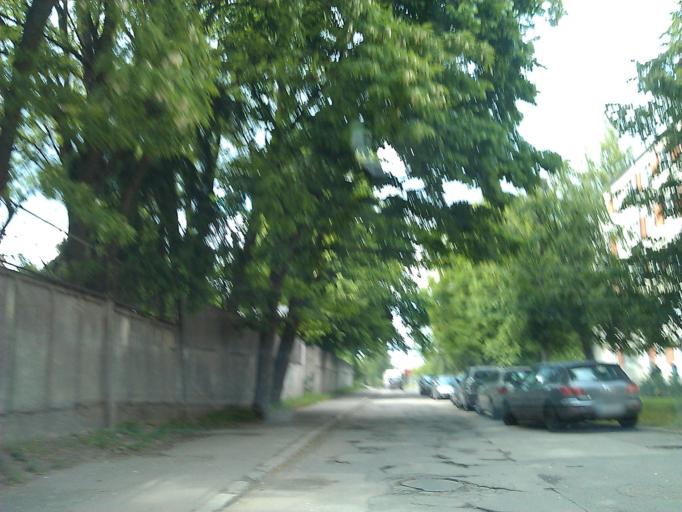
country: LV
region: Riga
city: Bergi
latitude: 56.9920
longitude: 24.2285
